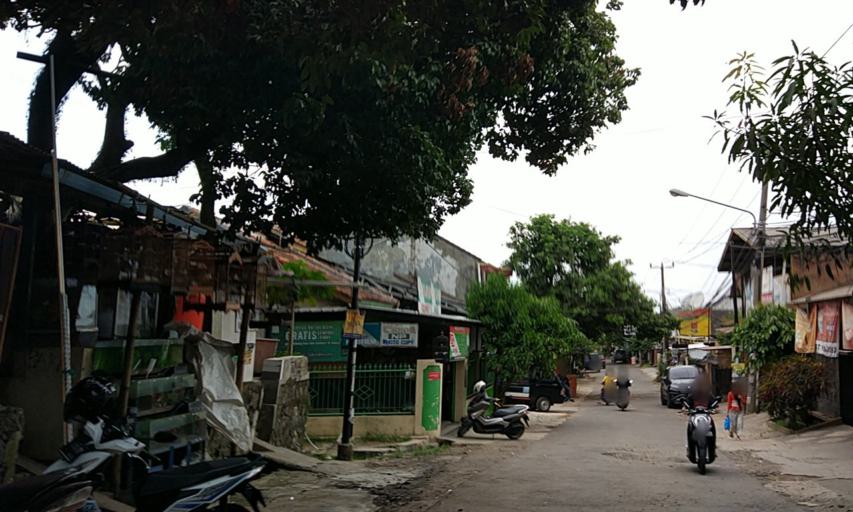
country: ID
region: West Java
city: Cileunyi
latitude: -6.9029
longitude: 107.6977
